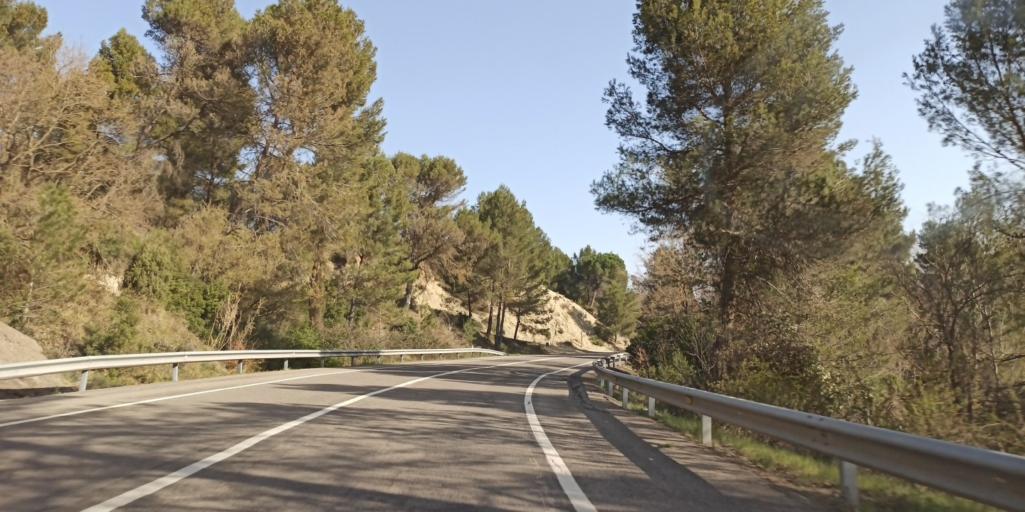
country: ES
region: Catalonia
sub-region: Provincia de Barcelona
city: Castelloli
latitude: 41.5933
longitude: 1.6826
